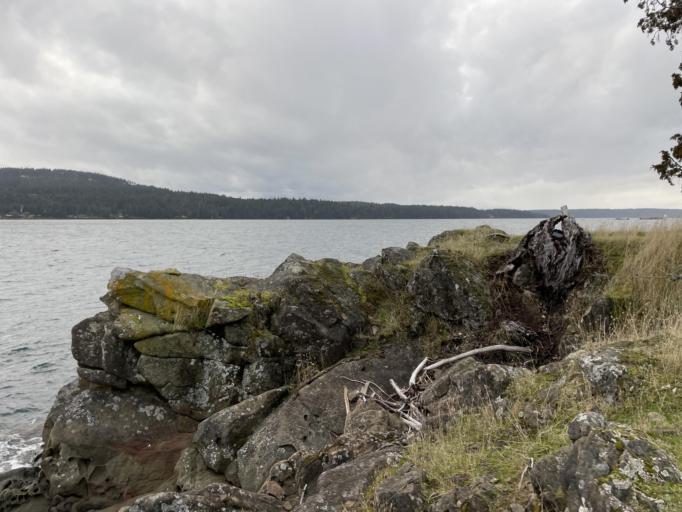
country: CA
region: British Columbia
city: North Cowichan
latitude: 48.9365
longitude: -123.5453
